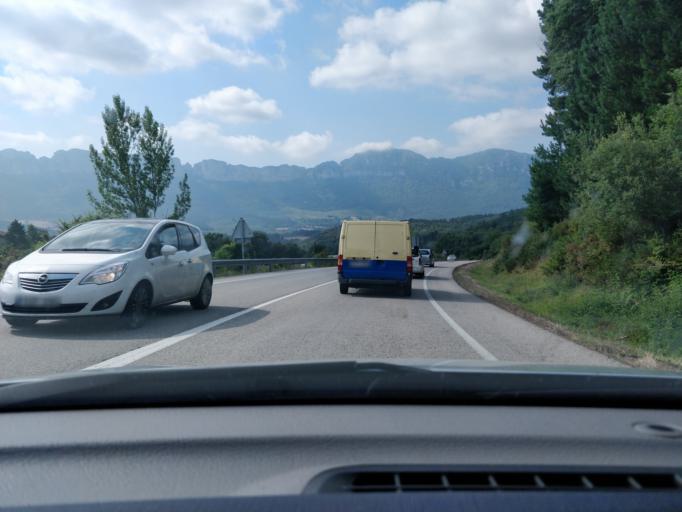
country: ES
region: Castille and Leon
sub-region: Provincia de Burgos
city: Villasana de Mena
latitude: 43.0998
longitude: -3.3063
